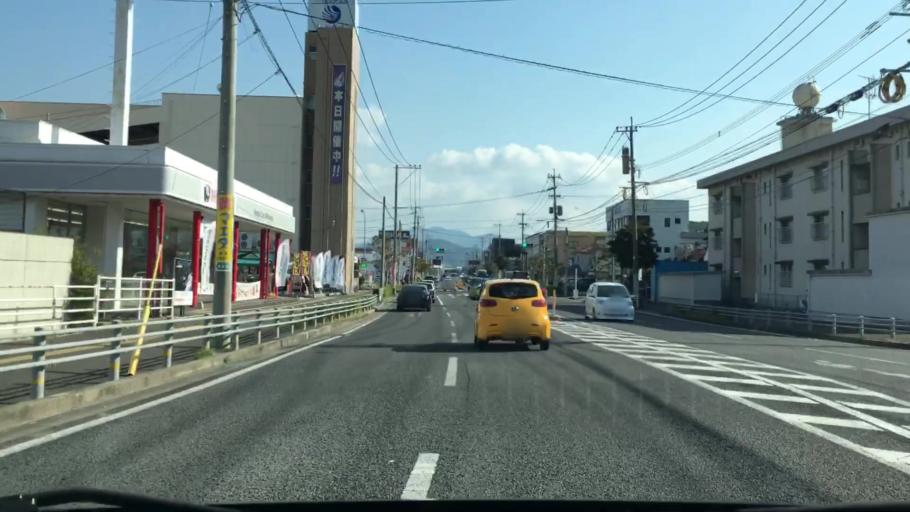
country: JP
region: Nagasaki
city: Togitsu
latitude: 32.8463
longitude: 129.8315
